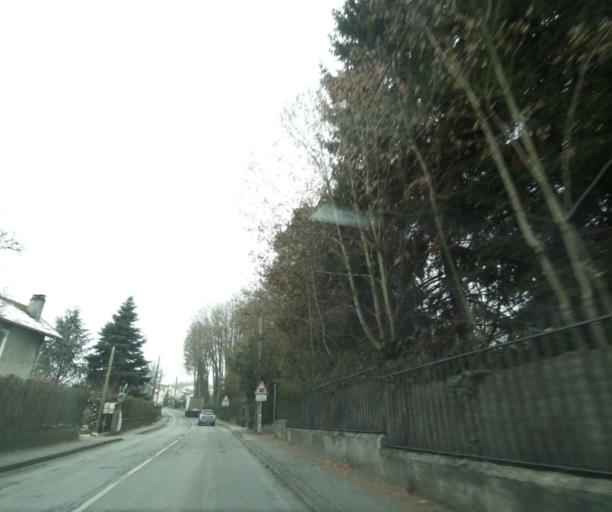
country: FR
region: Rhone-Alpes
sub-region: Departement de la Haute-Savoie
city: Reignier-Esery
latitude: 46.1278
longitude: 6.2665
